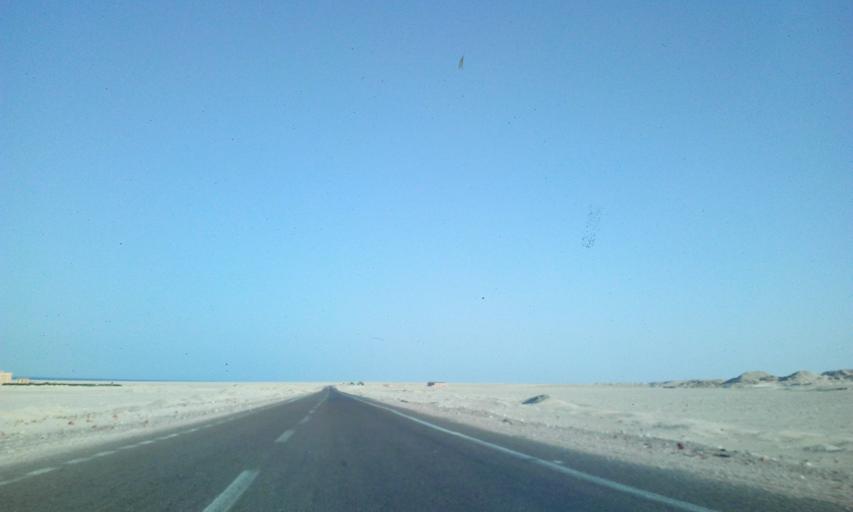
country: EG
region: As Suways
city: Ain Sukhna
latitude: 28.8498
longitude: 32.6914
